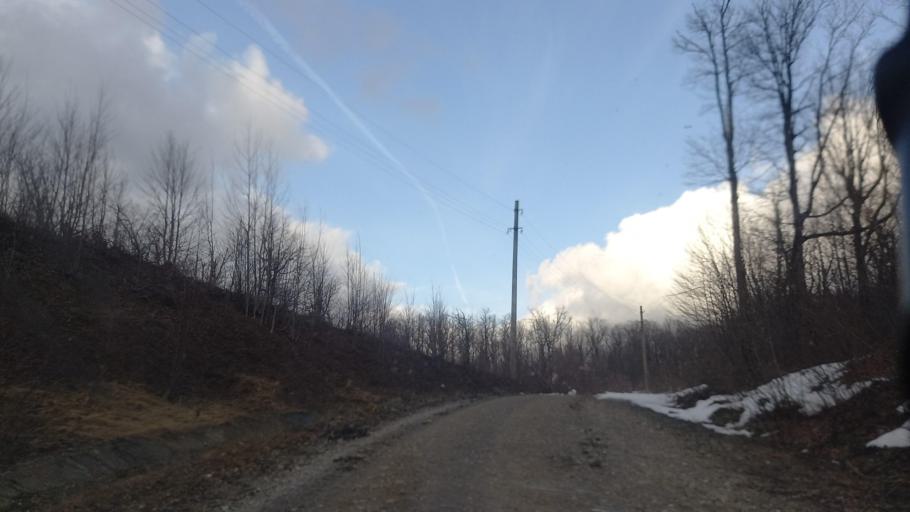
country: RU
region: Krasnodarskiy
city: Dzhubga
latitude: 44.5079
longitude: 38.7709
